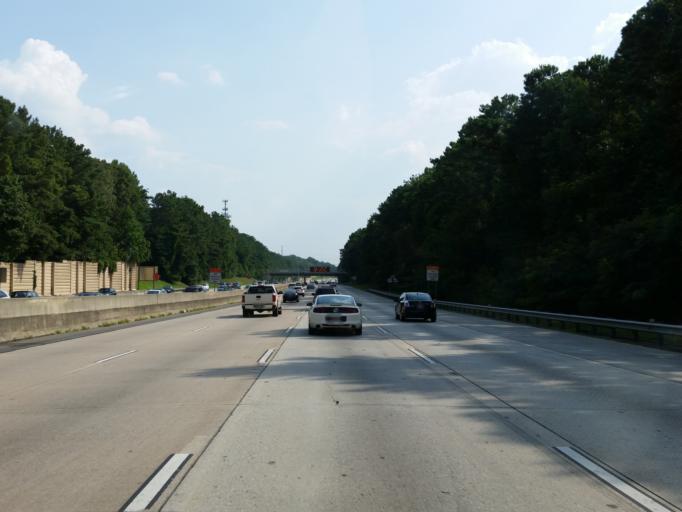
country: US
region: Georgia
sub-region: DeKalb County
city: Dunwoody
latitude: 33.9740
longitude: -84.3460
